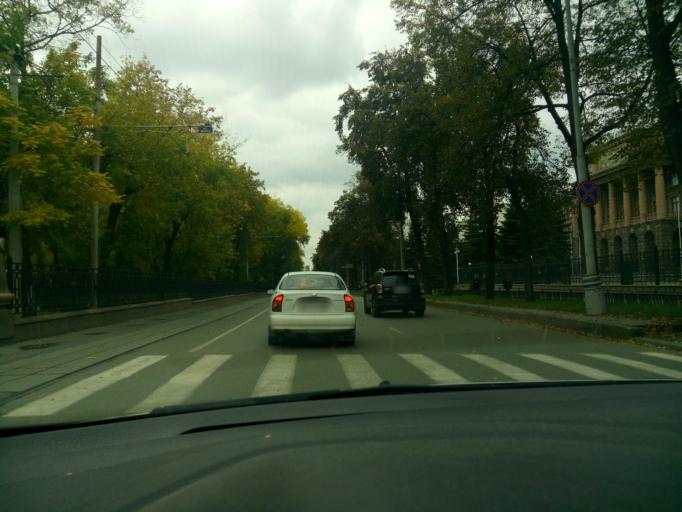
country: RU
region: Sverdlovsk
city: Yekaterinburg
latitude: 56.8410
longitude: 60.6260
